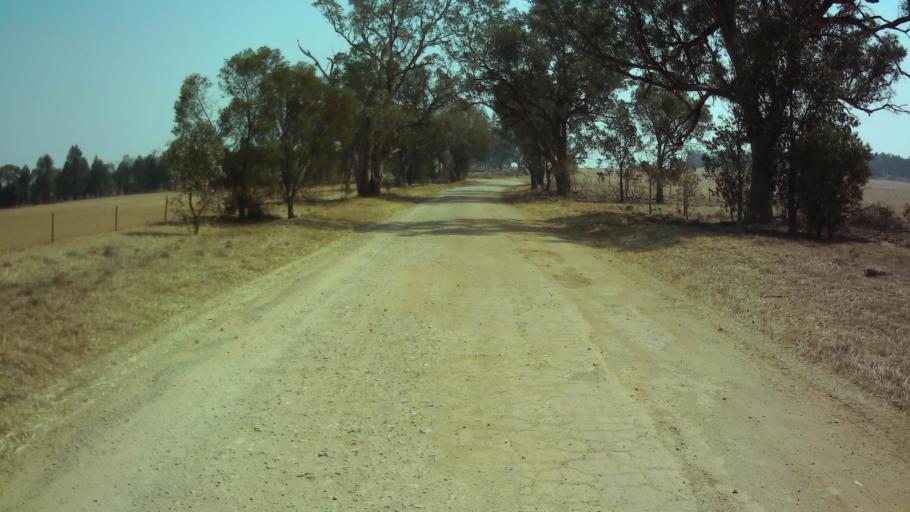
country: AU
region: New South Wales
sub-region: Weddin
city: Grenfell
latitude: -33.6480
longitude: 148.2701
